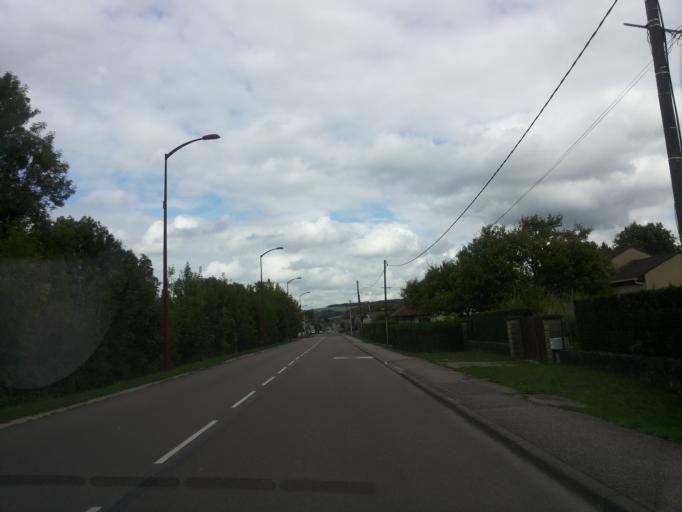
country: FR
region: Lorraine
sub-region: Departement de la Meuse
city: Ligny-en-Barrois
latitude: 48.6791
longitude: 5.3256
